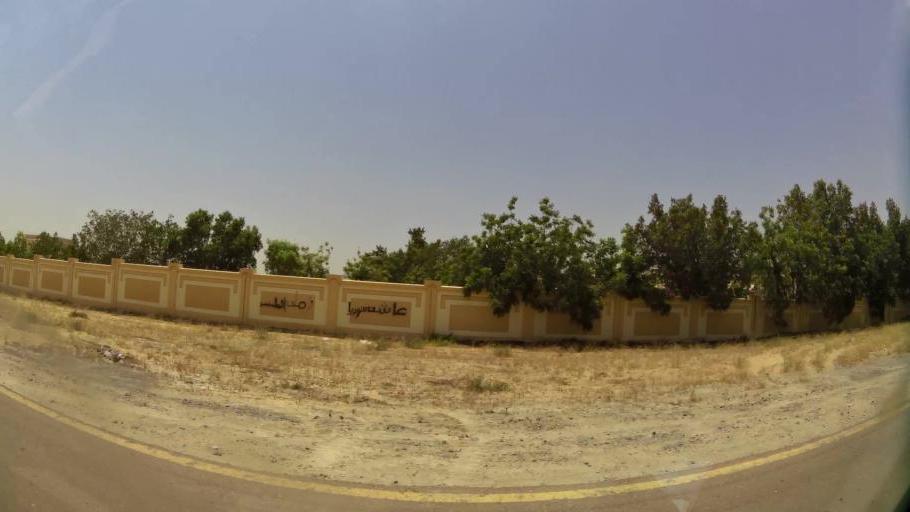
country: AE
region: Ajman
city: Ajman
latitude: 25.4217
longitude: 55.5046
